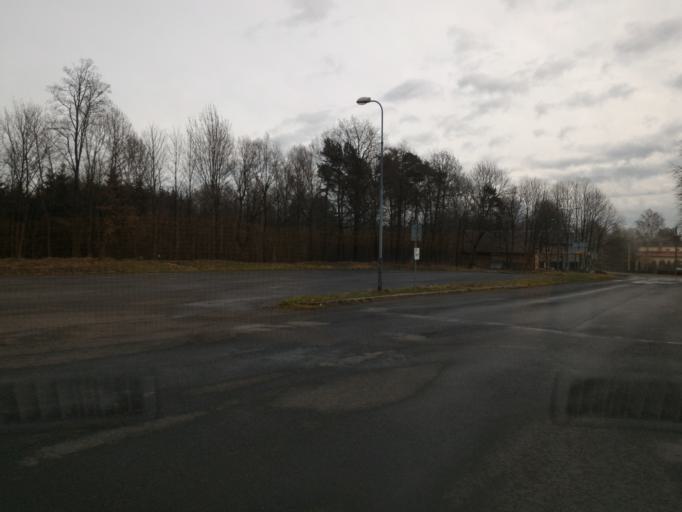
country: CZ
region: Ustecky
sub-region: Okres Decin
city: Rumburk
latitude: 50.9684
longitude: 14.5637
